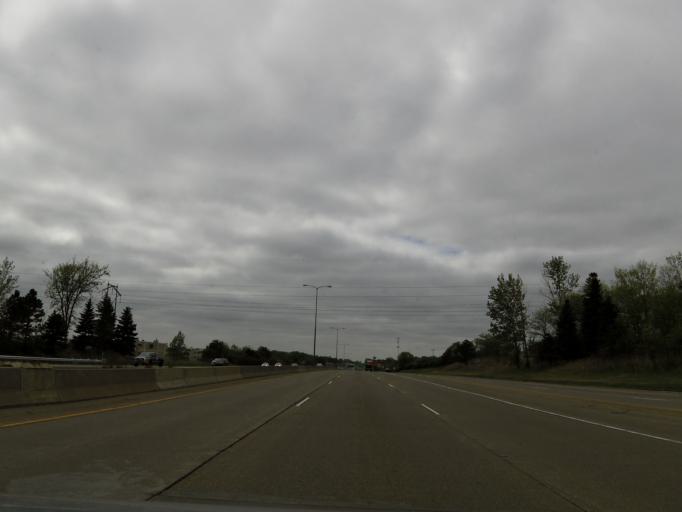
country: US
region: Minnesota
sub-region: Washington County
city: Oakdale
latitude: 44.9487
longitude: -92.9631
